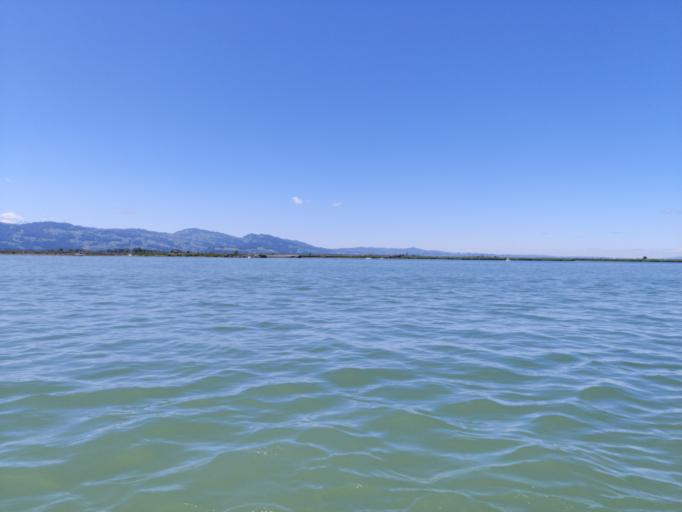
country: DE
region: Bavaria
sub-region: Swabia
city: Lindau
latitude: 47.5194
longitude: 9.6630
